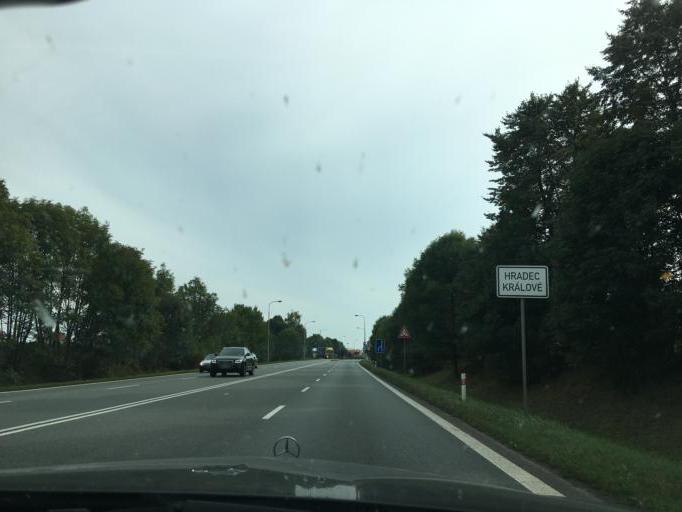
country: CZ
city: Predmerice nad Labem
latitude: 50.2243
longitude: 15.7895
